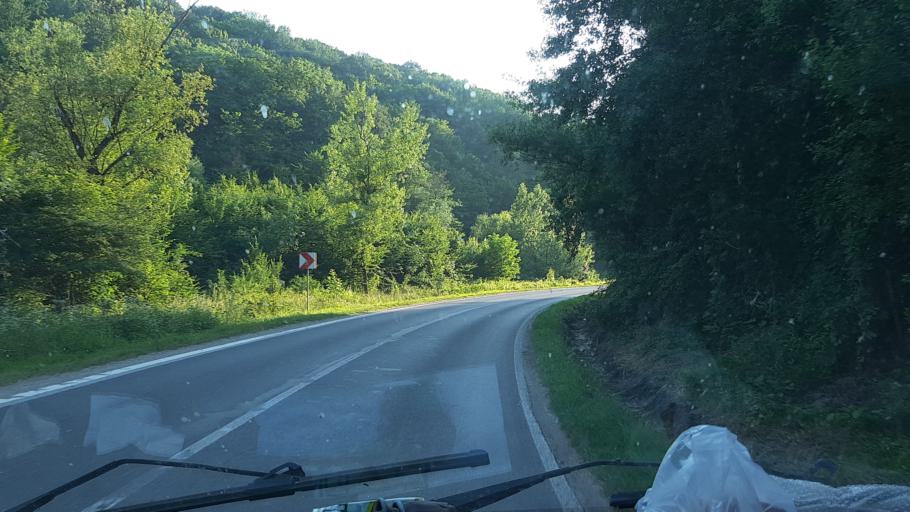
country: RO
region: Caras-Severin
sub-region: Municipiul Resita
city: Calnic
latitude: 45.3433
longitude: 21.8370
